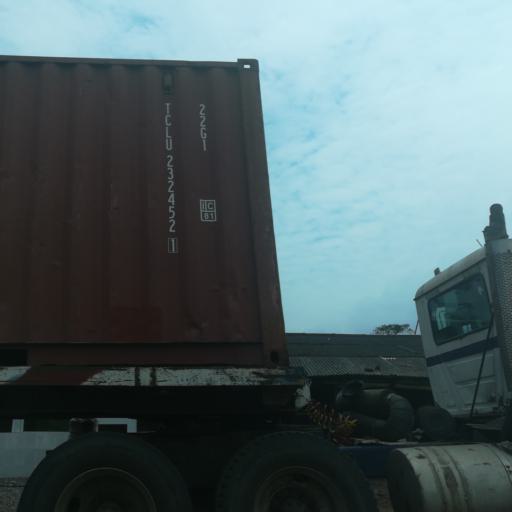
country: NG
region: Lagos
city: Ejirin
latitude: 6.6594
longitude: 3.7945
